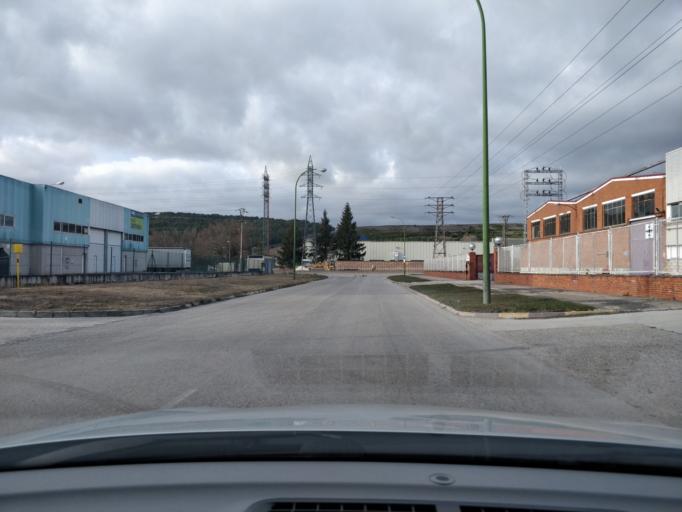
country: ES
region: Castille and Leon
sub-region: Provincia de Burgos
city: Villalbilla de Burgos
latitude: 42.3635
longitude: -3.7579
